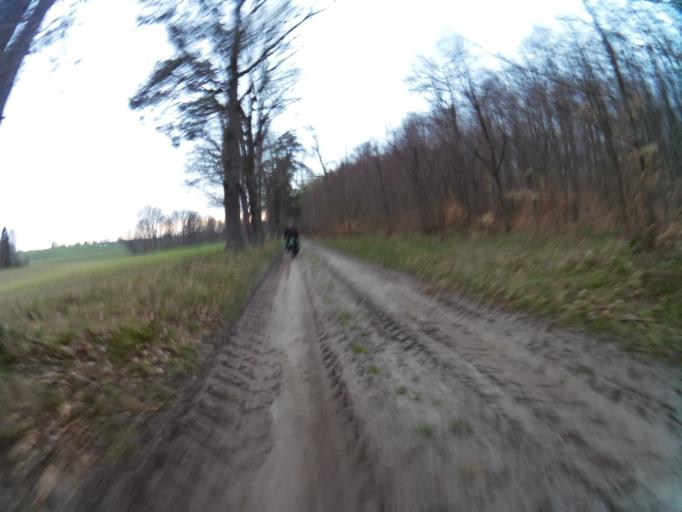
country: PL
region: West Pomeranian Voivodeship
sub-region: Powiat szczecinecki
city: Borne Sulinowo
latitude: 53.6684
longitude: 16.5410
